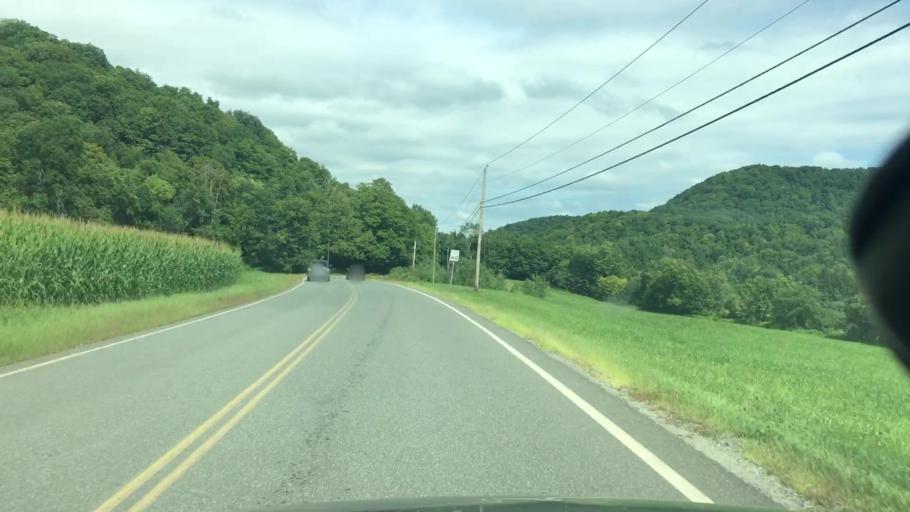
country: US
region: Massachusetts
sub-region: Franklin County
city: Colrain
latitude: 42.6991
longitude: -72.6955
